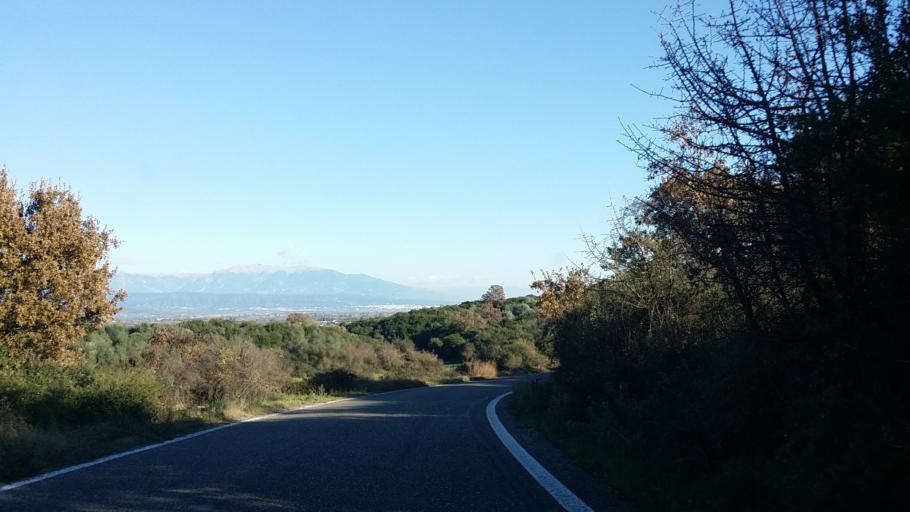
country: GR
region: West Greece
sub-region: Nomos Aitolias kai Akarnanias
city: Fitiai
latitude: 38.6233
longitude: 21.2100
